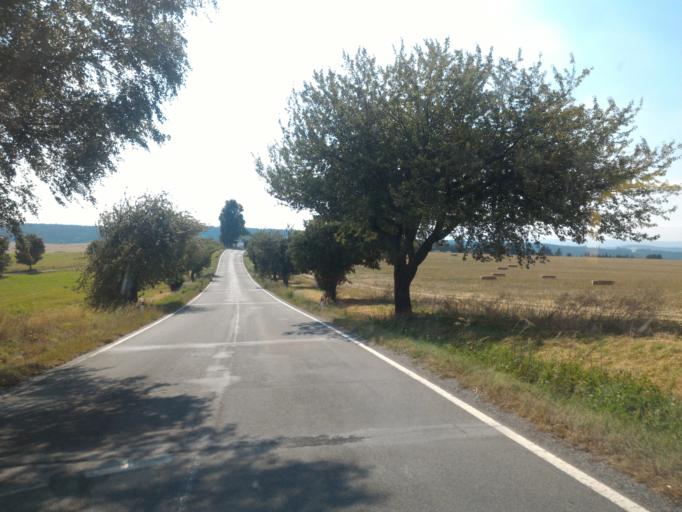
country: CZ
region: Vysocina
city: Bohdalov
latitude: 49.4604
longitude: 15.8147
